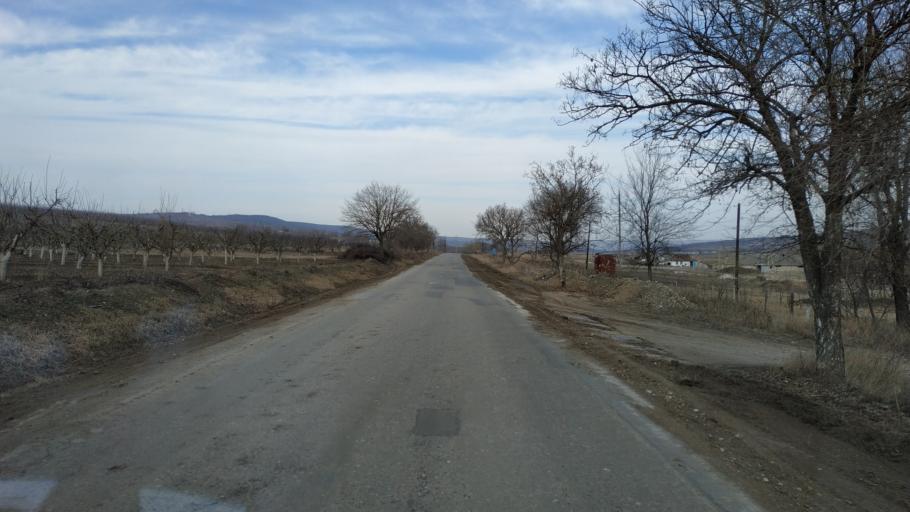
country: MD
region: Nisporeni
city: Nisporeni
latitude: 47.0833
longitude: 28.1427
